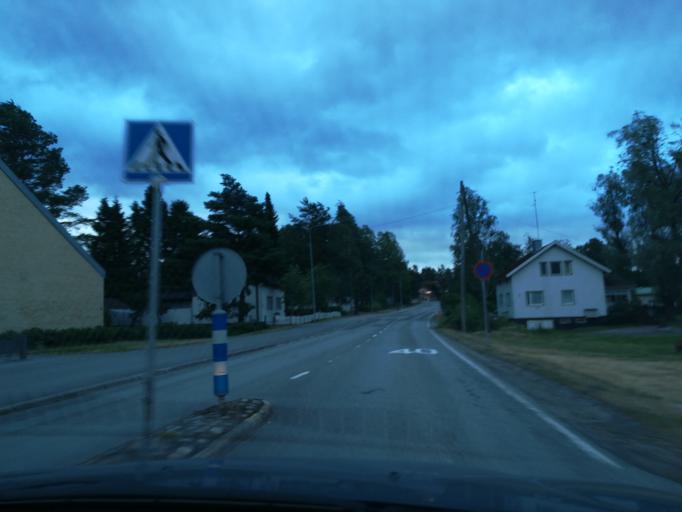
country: FI
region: Southern Savonia
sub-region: Mikkeli
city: Ristiina
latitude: 61.5064
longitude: 27.2581
